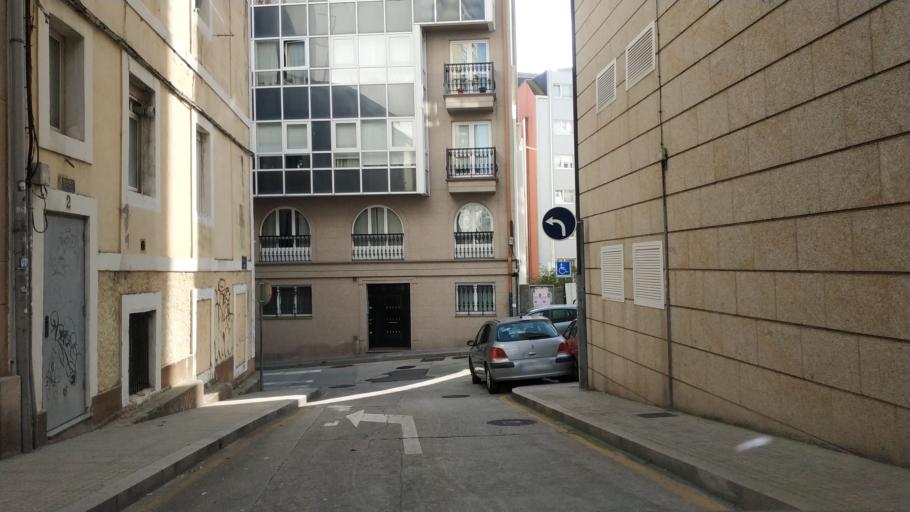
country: ES
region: Galicia
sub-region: Provincia da Coruna
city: A Coruna
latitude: 43.3750
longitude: -8.3960
